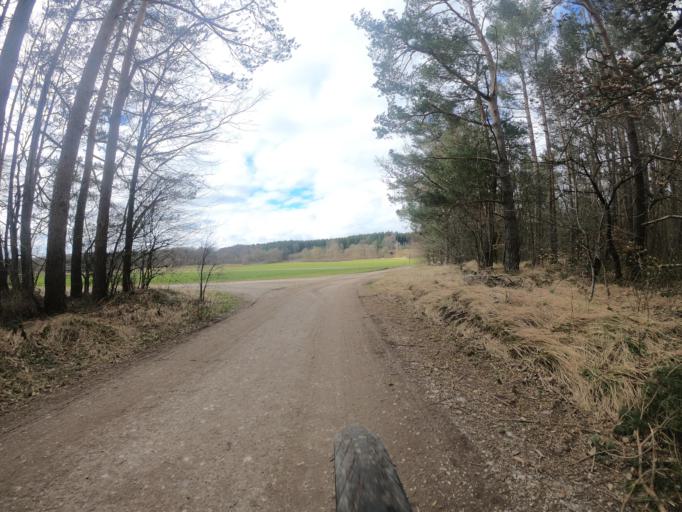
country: DE
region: Bavaria
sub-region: Upper Bavaria
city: Schongeising
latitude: 48.1644
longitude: 11.2035
